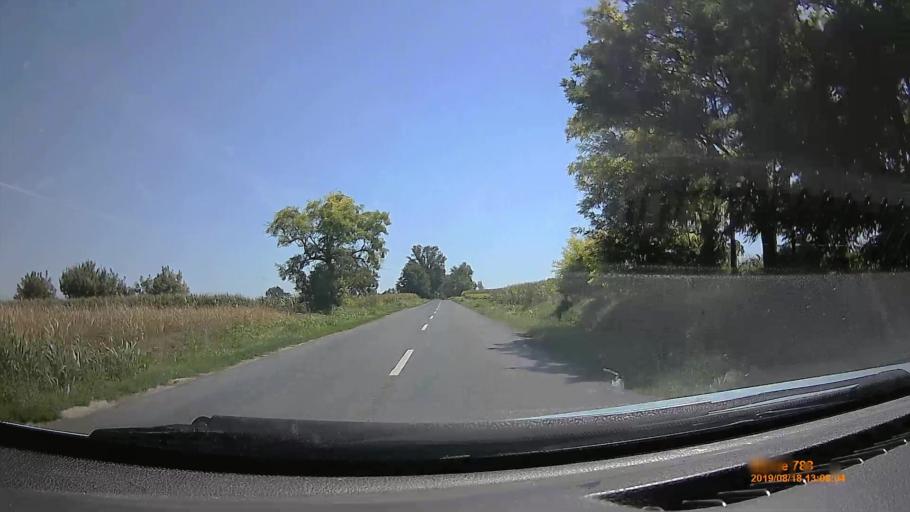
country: HU
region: Fejer
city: Kaloz
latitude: 46.9433
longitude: 18.4990
